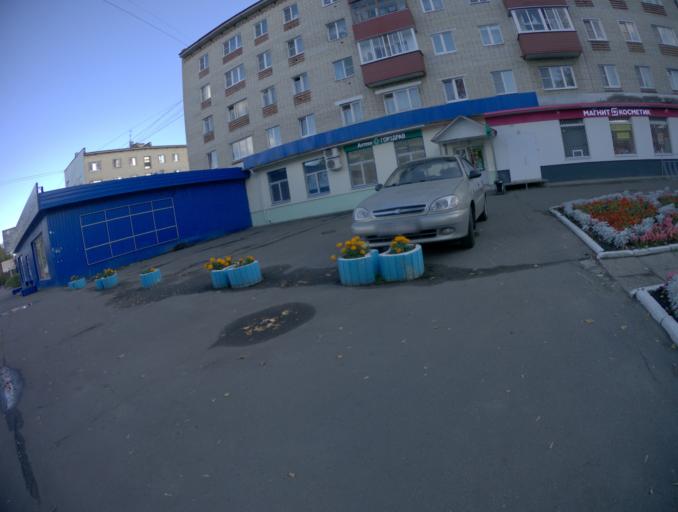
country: RU
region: Moskovskaya
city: Shatura
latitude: 55.5756
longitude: 39.5336
